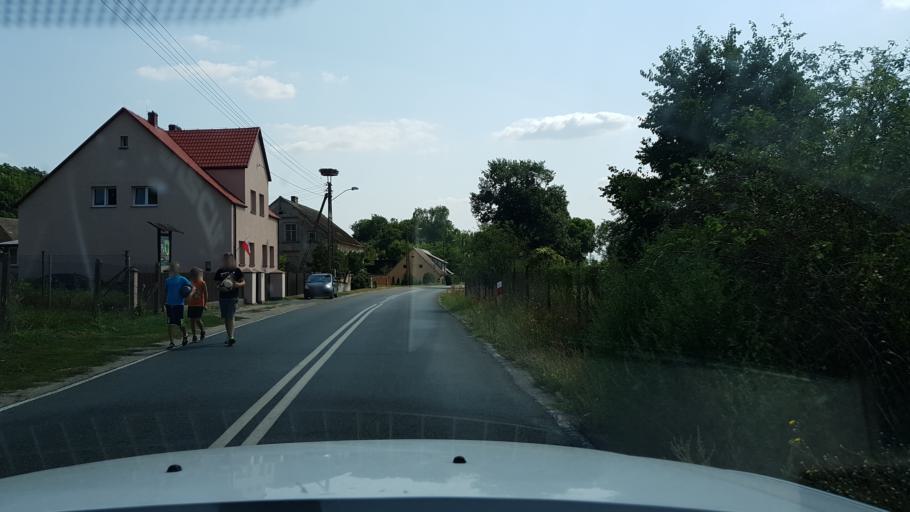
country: PL
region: West Pomeranian Voivodeship
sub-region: Powiat gryfinski
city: Cedynia
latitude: 52.8084
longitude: 14.2445
